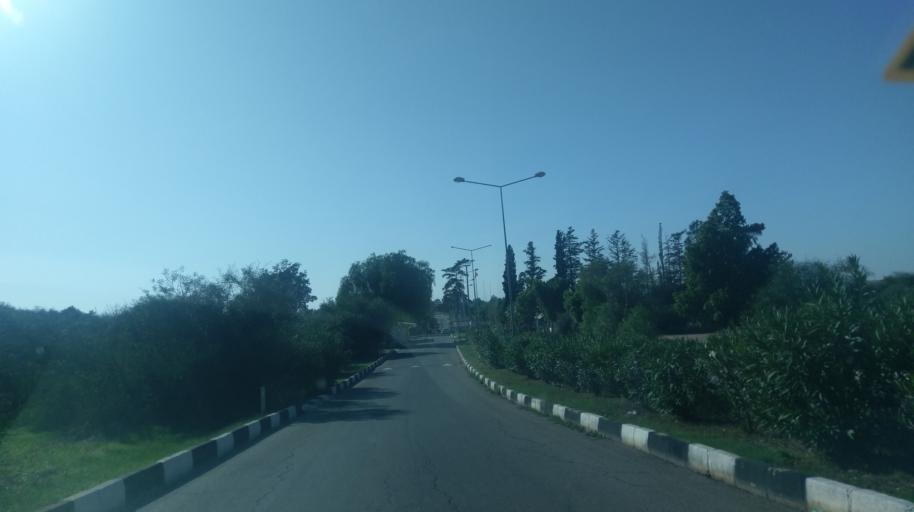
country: CY
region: Ammochostos
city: Famagusta
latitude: 35.0969
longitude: 33.9040
